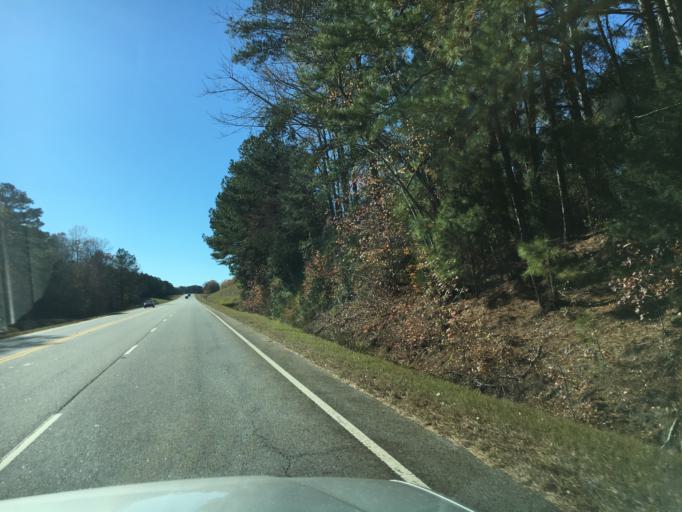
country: US
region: Georgia
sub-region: Hart County
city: Hartwell
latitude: 34.3441
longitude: -82.8263
